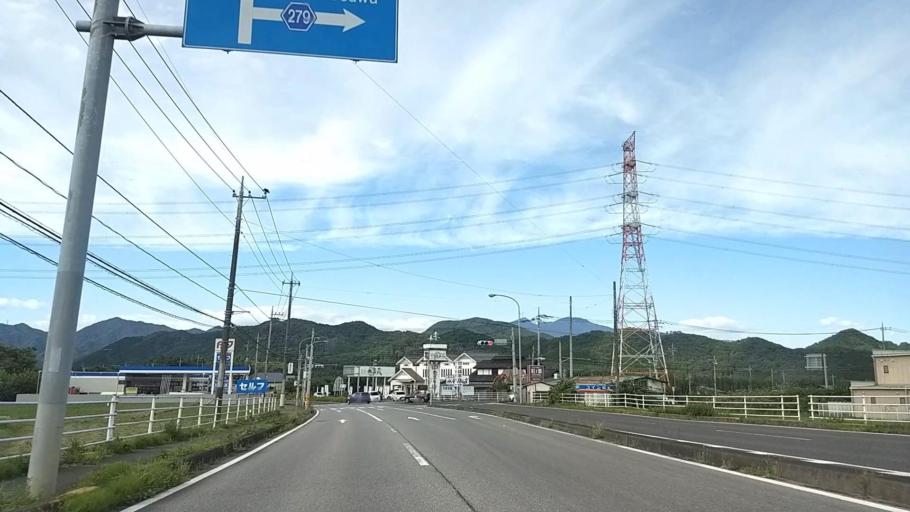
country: JP
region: Tochigi
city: Imaichi
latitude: 36.7651
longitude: 139.7168
